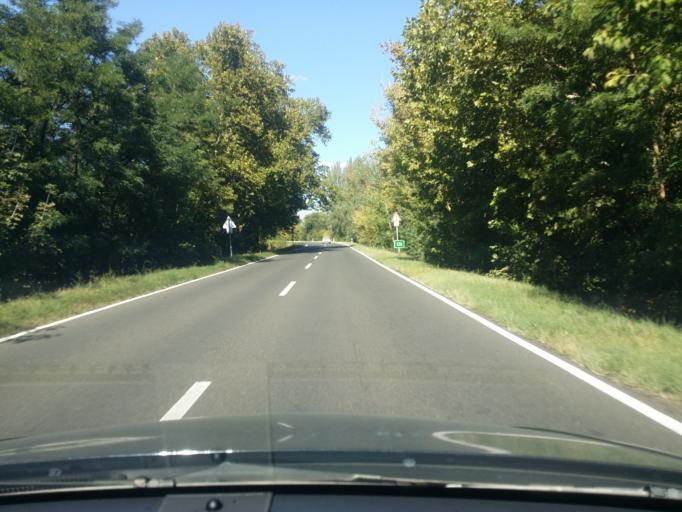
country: HU
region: Bacs-Kiskun
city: Palmonostora
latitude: 46.6042
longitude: 19.9188
